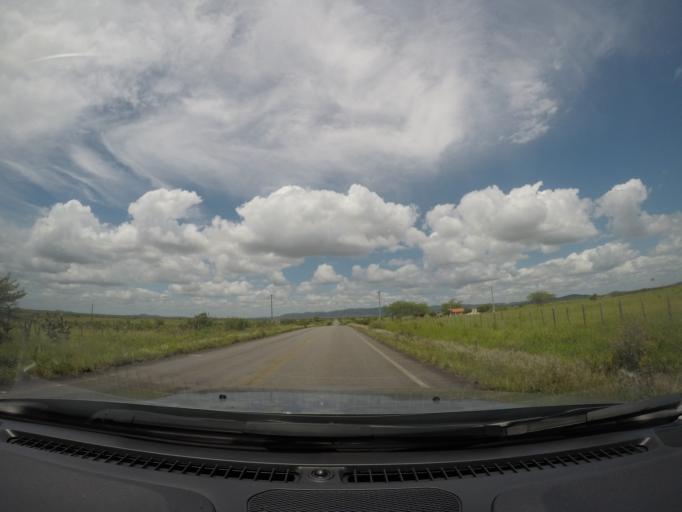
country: BR
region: Bahia
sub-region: Ipira
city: Ipira
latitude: -12.2190
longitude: -39.7869
